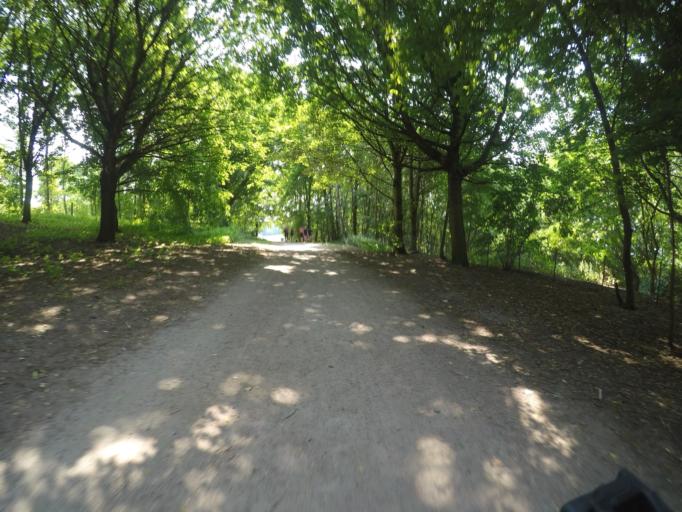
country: DE
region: Schleswig-Holstein
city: Barsbuettel
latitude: 53.5604
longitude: 10.1452
